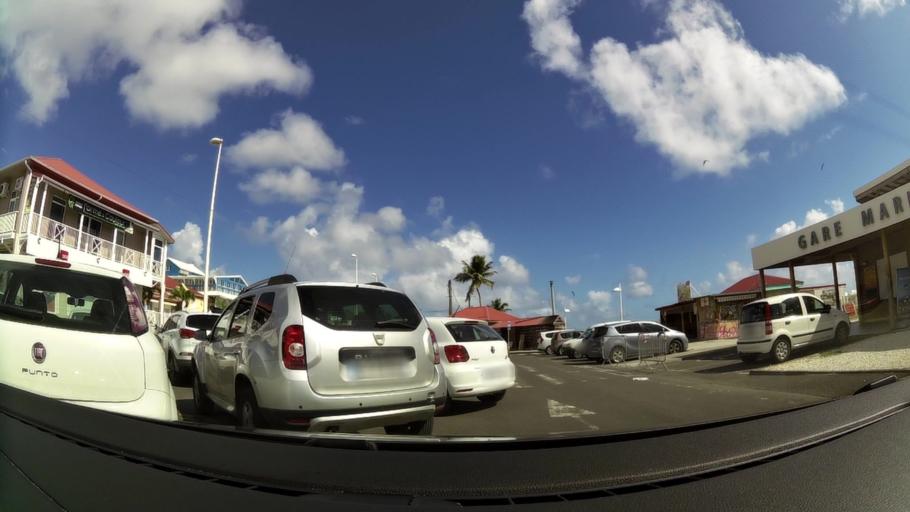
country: GP
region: Guadeloupe
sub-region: Guadeloupe
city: Saint-Francois
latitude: 16.2504
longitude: -61.2730
